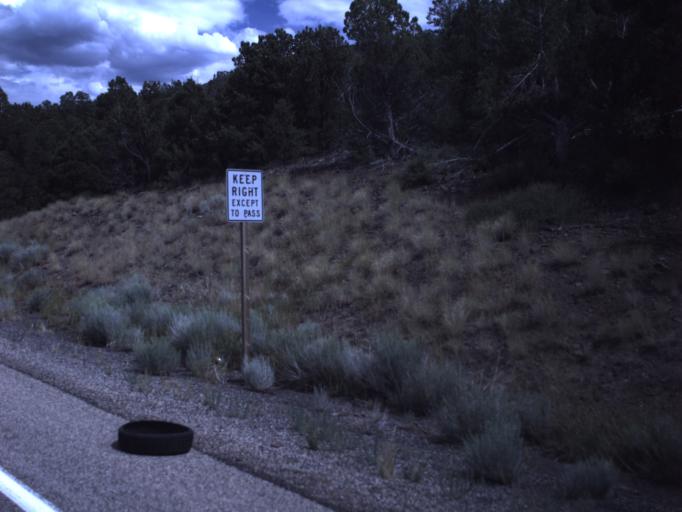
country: US
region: Utah
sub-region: Beaver County
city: Beaver
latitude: 38.0610
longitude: -112.6264
